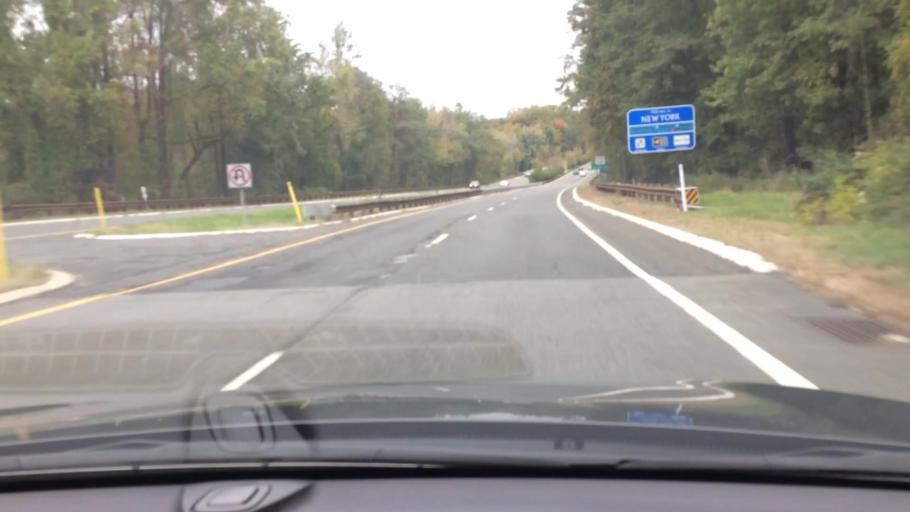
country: US
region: New York
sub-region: Rockland County
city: Sparkill
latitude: 41.0047
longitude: -73.9198
